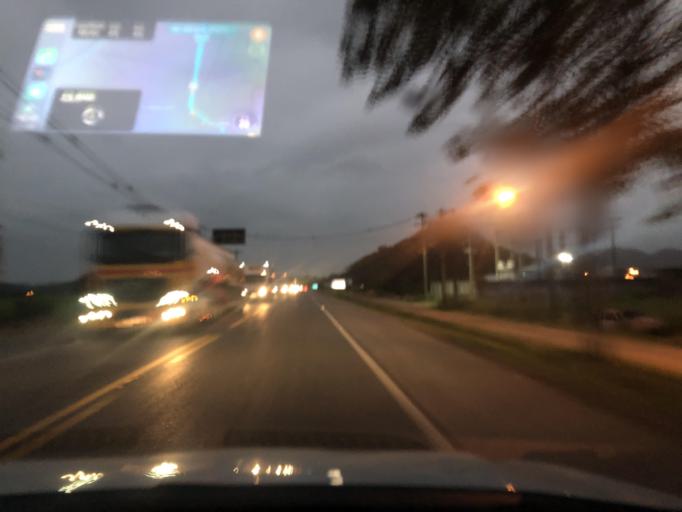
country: BR
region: Santa Catarina
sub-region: Jaragua Do Sul
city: Jaragua do Sul
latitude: -26.6100
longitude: -49.0098
